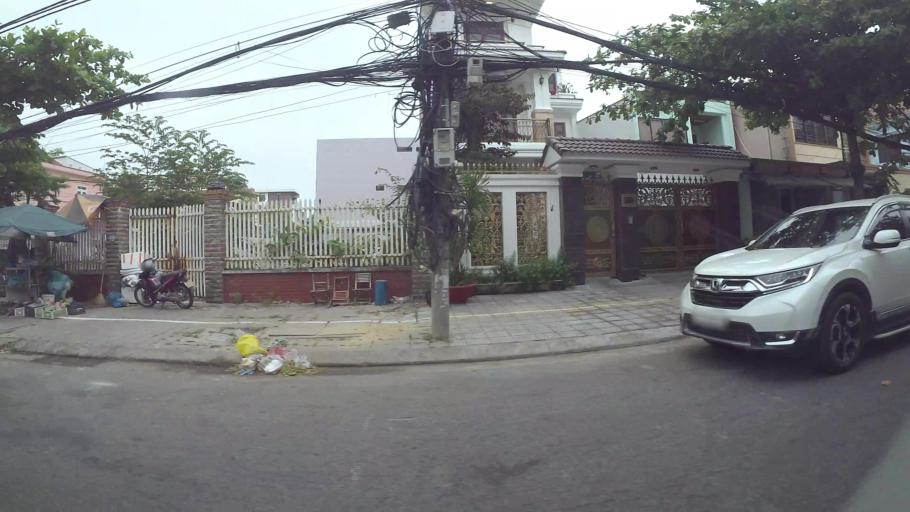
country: VN
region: Da Nang
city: Cam Le
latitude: 16.0440
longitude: 108.2081
